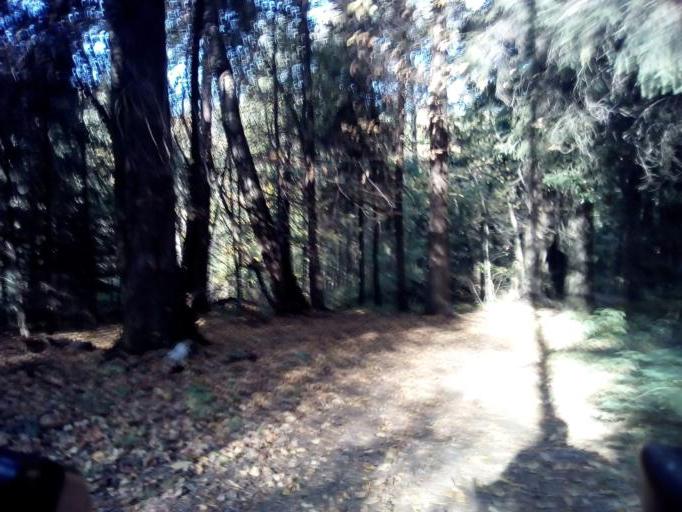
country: RU
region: Moskovskaya
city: Ramenskoye
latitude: 55.5752
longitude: 38.3125
